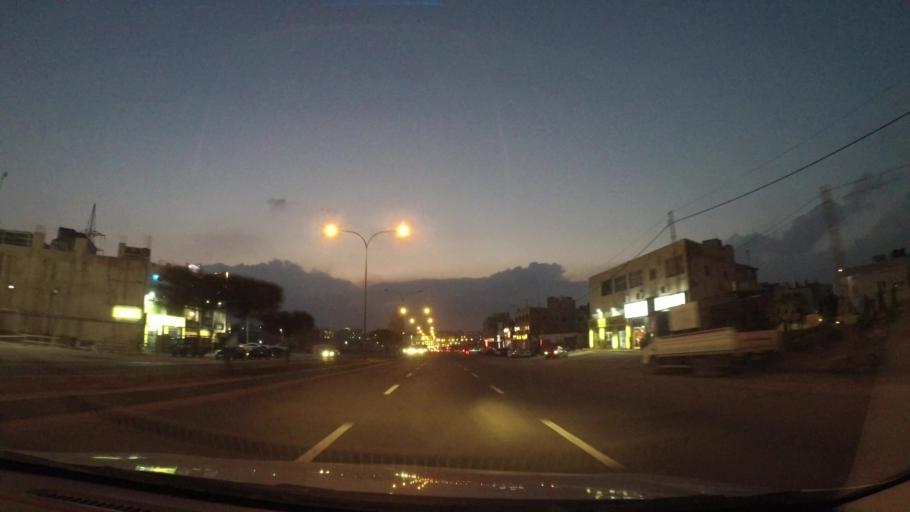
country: JO
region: Amman
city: Al Bunayyat ash Shamaliyah
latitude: 31.8961
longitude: 35.9084
